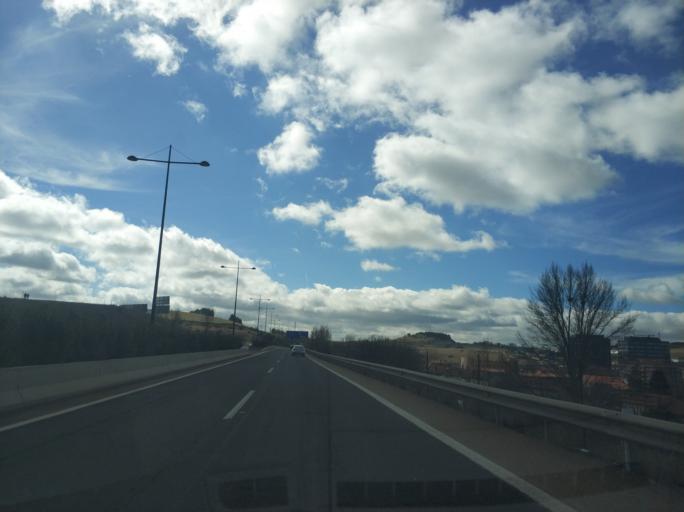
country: ES
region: Castille and Leon
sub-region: Provincia de Burgos
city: Burgos
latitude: 42.3312
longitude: -3.6968
